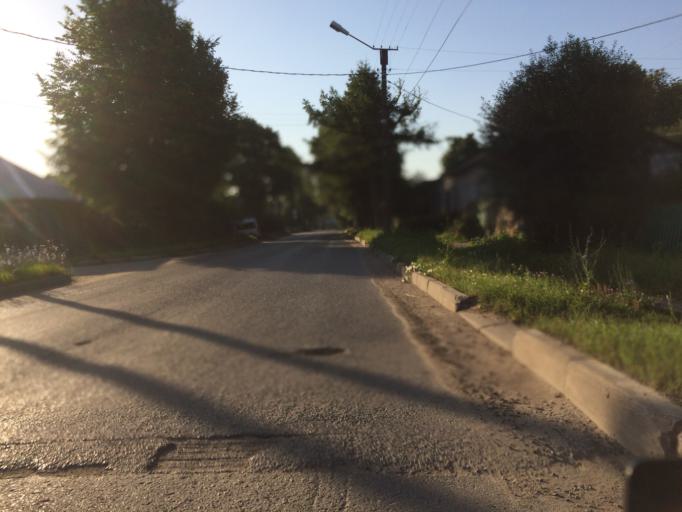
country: RU
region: Mariy-El
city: Yoshkar-Ola
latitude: 56.6515
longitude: 47.9015
